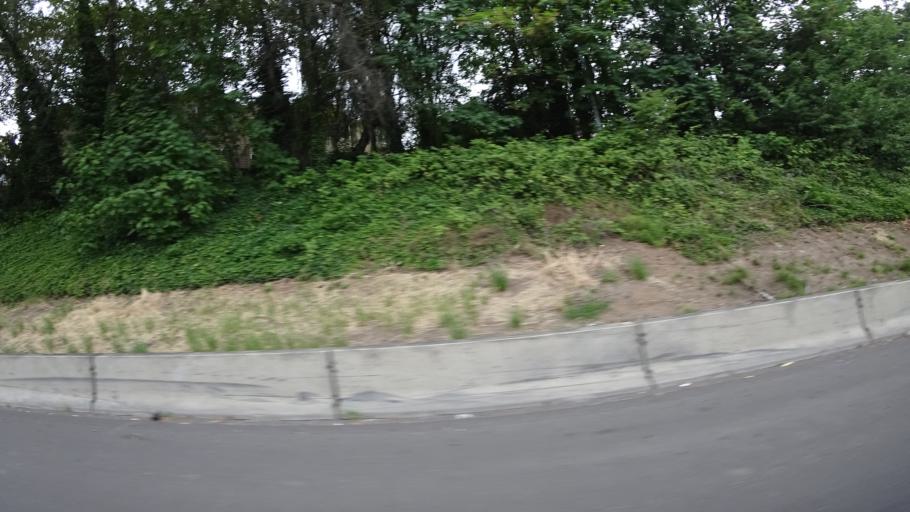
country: US
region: Oregon
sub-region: Multnomah County
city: Portland
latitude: 45.4882
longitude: -122.6781
